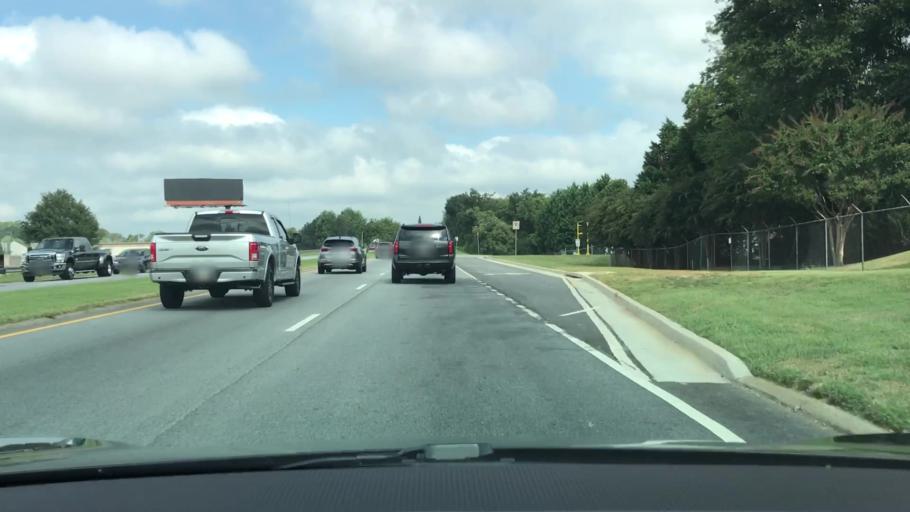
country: US
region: Georgia
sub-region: Hall County
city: Gainesville
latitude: 34.2896
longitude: -83.8126
